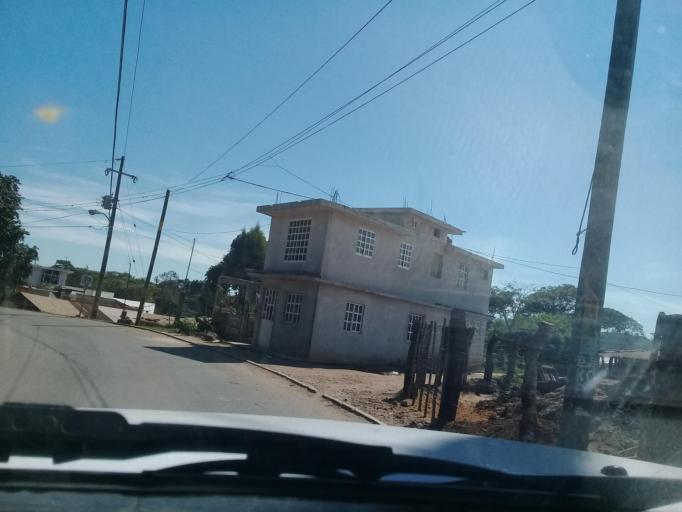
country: MX
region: Veracruz
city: El Castillo
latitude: 19.5509
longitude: -96.8538
